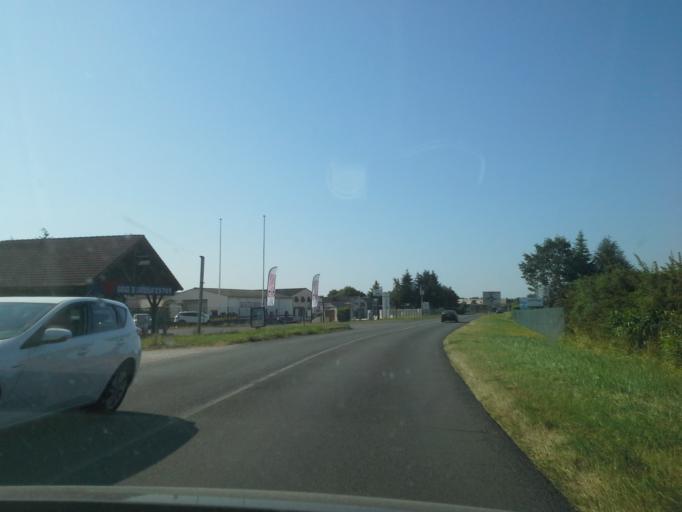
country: FR
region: Centre
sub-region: Departement du Loir-et-Cher
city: Les Montils
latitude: 47.5138
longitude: 1.3004
